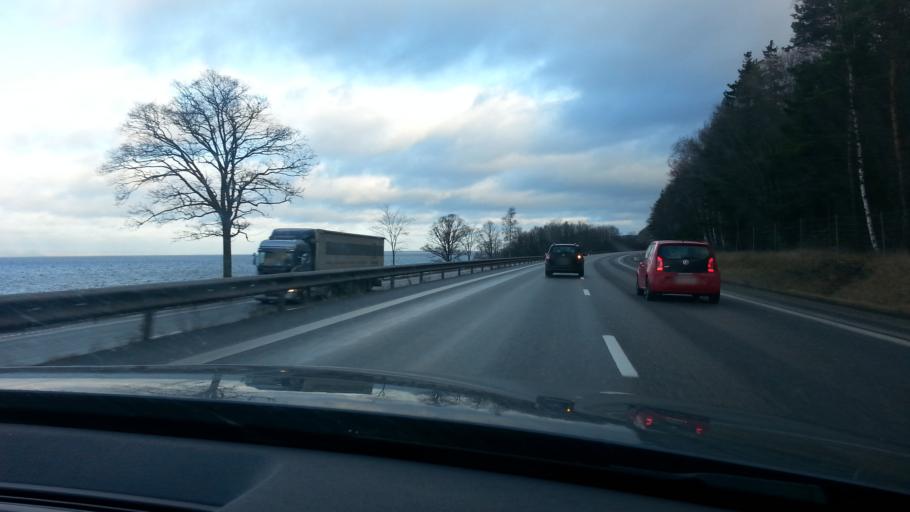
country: SE
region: Joenkoeping
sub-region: Jonkopings Kommun
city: Kaxholmen
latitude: 57.8863
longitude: 14.2837
